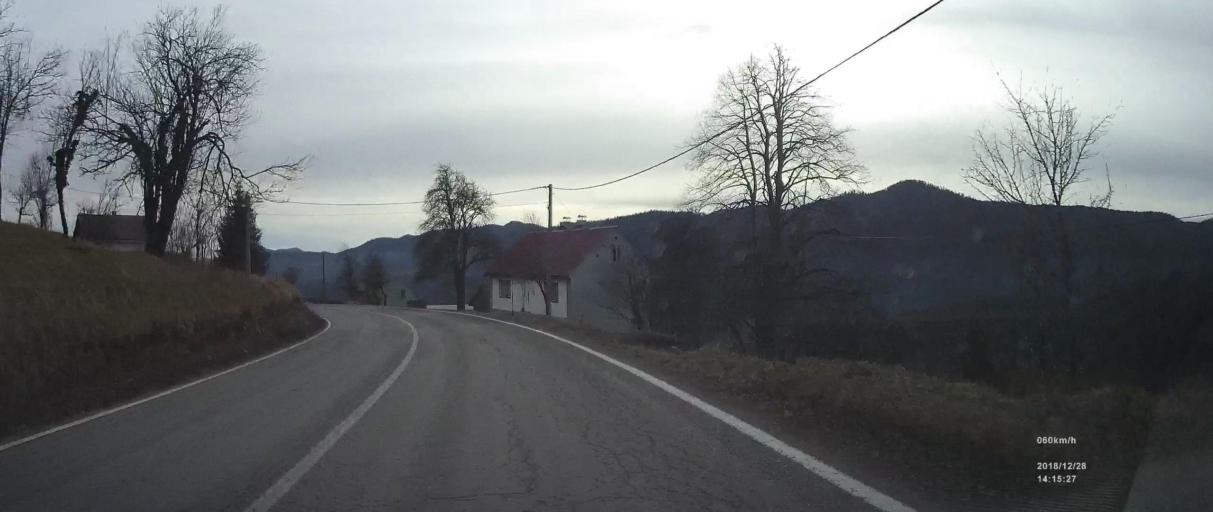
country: HR
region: Primorsko-Goranska
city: Vrbovsko
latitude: 45.4238
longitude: 15.0268
